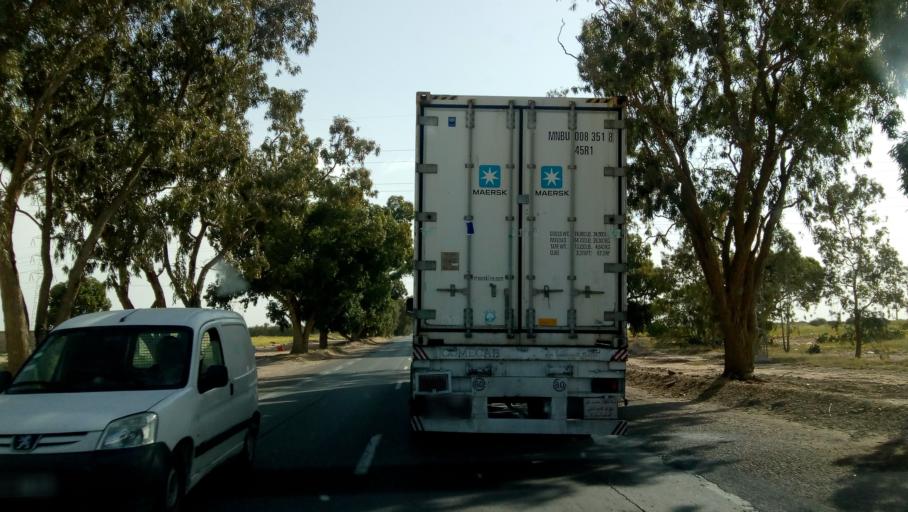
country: TN
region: Qabis
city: Gabes
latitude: 33.8917
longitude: 10.0348
